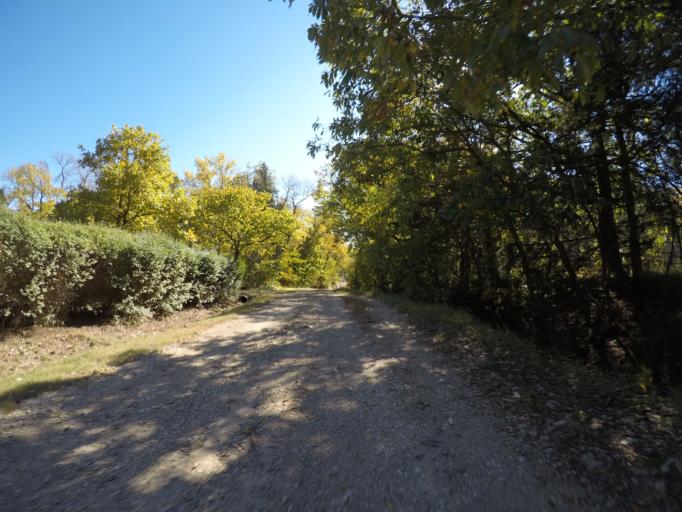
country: US
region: Kansas
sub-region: Wabaunsee County
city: Alma
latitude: 38.9806
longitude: -96.4555
